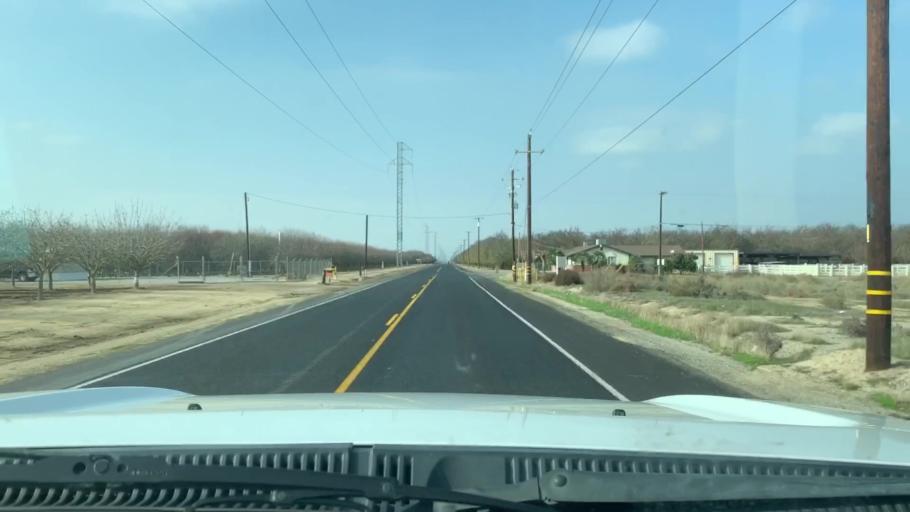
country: US
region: California
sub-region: Kern County
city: Shafter
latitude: 35.4418
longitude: -119.2957
